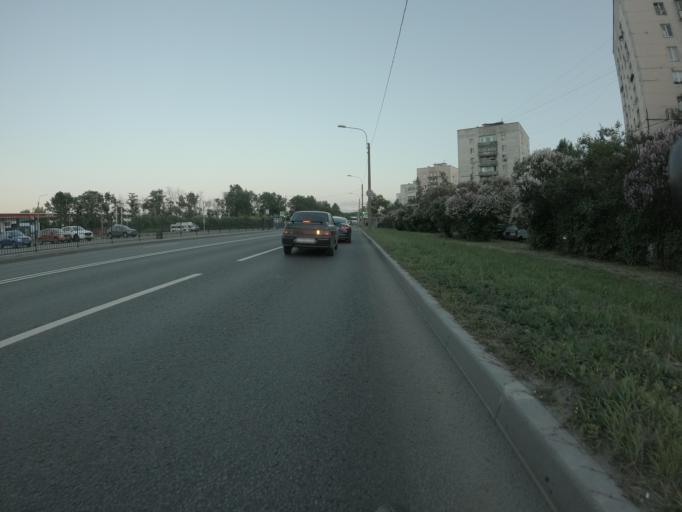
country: RU
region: St.-Petersburg
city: Dachnoye
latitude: 59.8483
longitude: 30.2803
